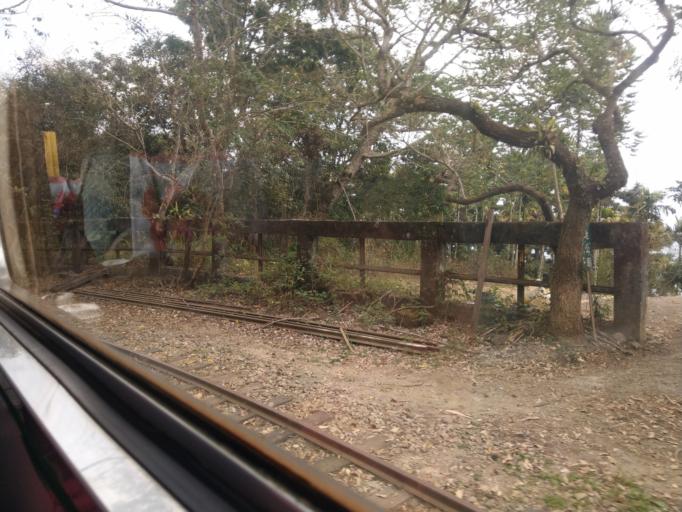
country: TW
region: Taiwan
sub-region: Chiayi
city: Jiayi Shi
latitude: 23.5414
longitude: 120.6206
